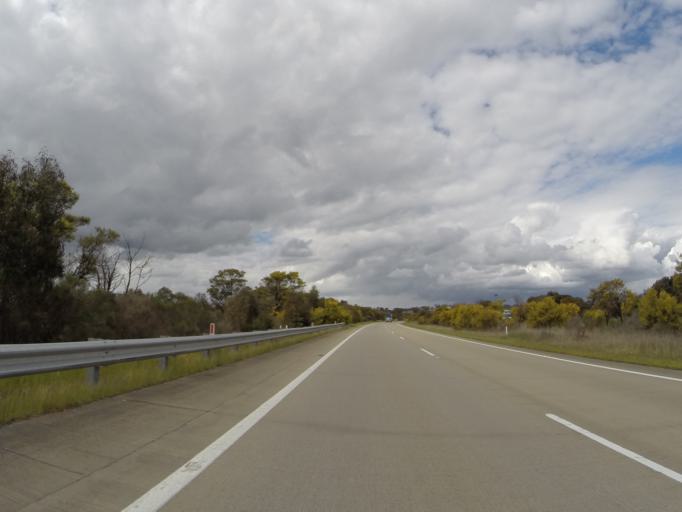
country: AU
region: New South Wales
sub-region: Goulburn Mulwaree
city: Goulburn
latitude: -34.8123
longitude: 149.4724
